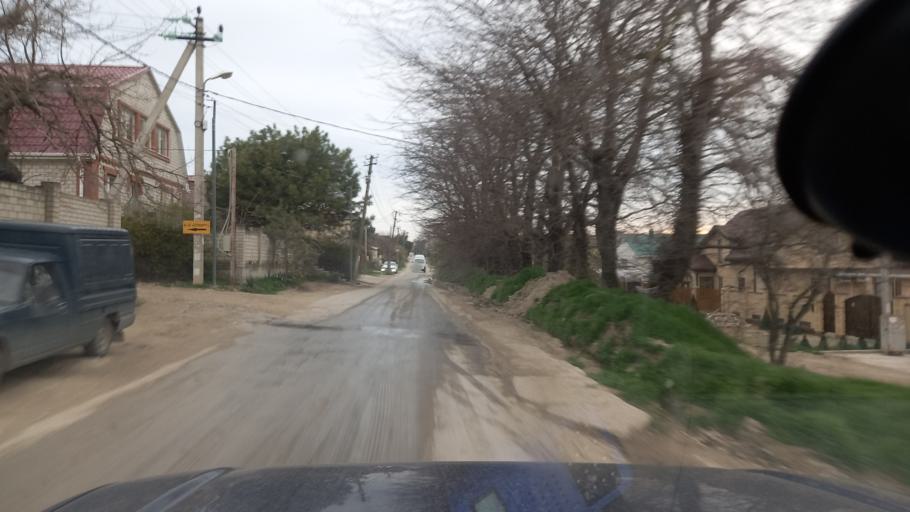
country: RU
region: Krasnodarskiy
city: Anapskaya
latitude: 44.8501
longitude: 37.3598
